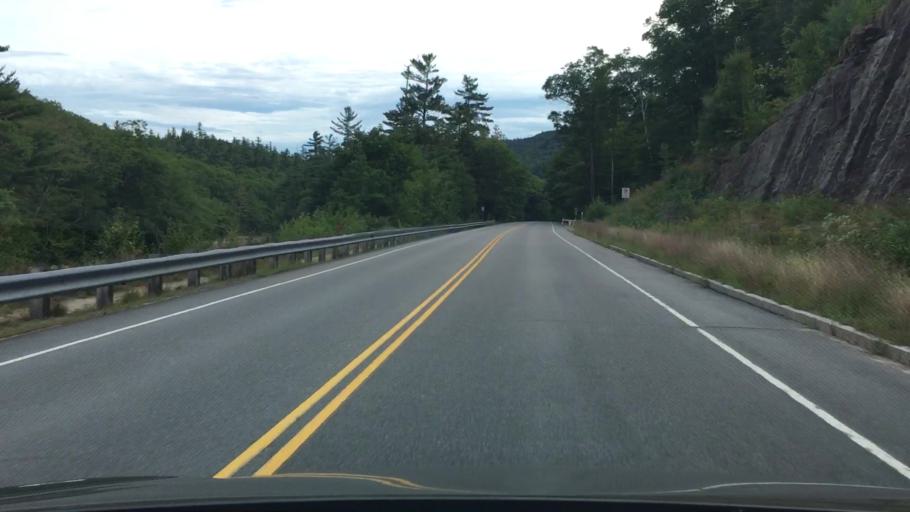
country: US
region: New Hampshire
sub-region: Carroll County
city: North Conway
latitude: 44.0141
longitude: -71.2450
